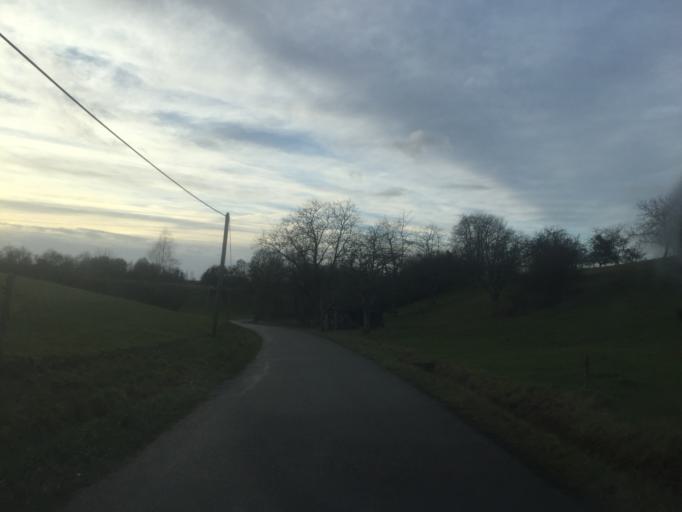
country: FR
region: Franche-Comte
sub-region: Departement du Jura
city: Orchamps
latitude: 47.1307
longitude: 5.6980
